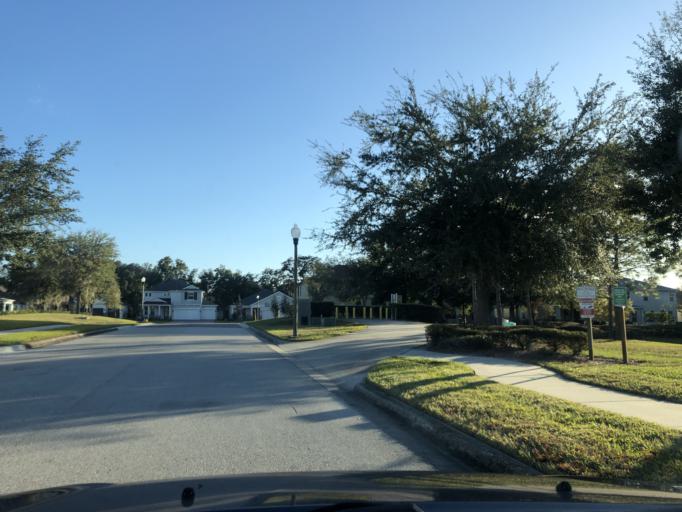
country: US
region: Florida
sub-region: Seminole County
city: Goldenrod
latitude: 28.6130
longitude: -81.2620
